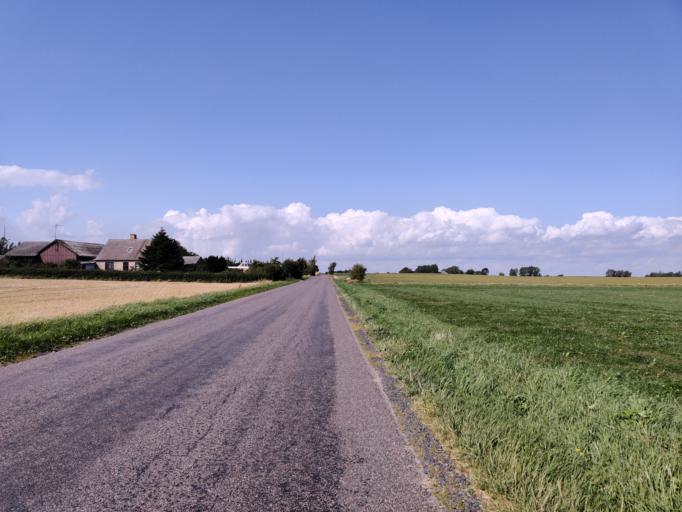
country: DK
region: Zealand
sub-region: Guldborgsund Kommune
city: Nykobing Falster
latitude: 54.6065
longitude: 11.9267
